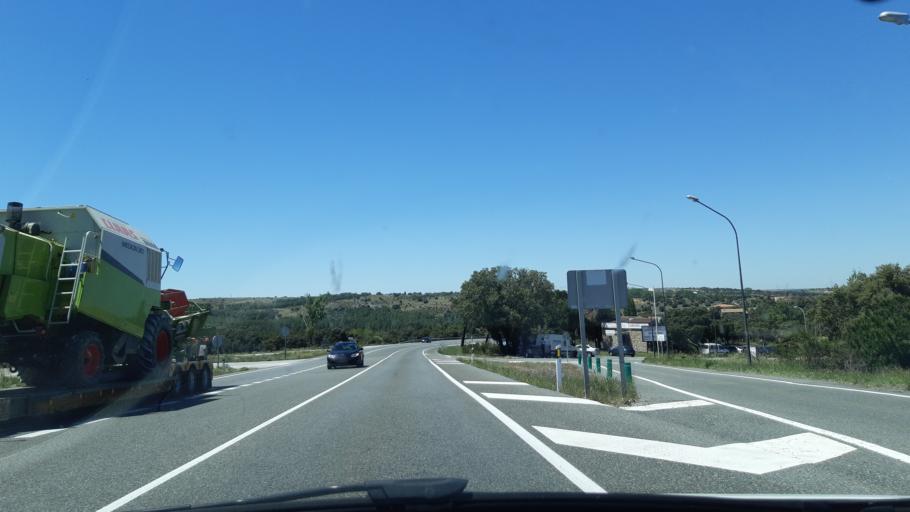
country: ES
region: Castille and Leon
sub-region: Provincia de Segovia
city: Ituero y Lama
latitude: 40.7689
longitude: -4.3674
